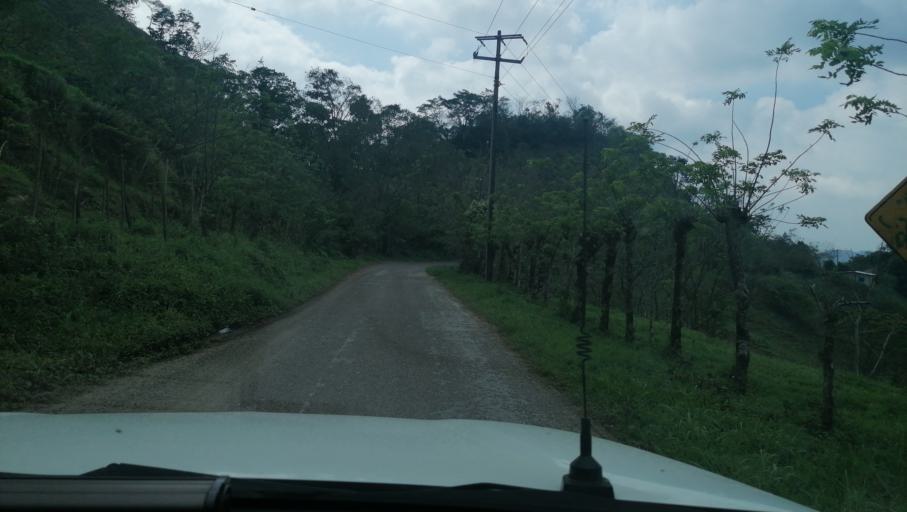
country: MX
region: Chiapas
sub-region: Francisco Leon
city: San Miguel la Sardina
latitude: 17.2371
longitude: -93.3133
